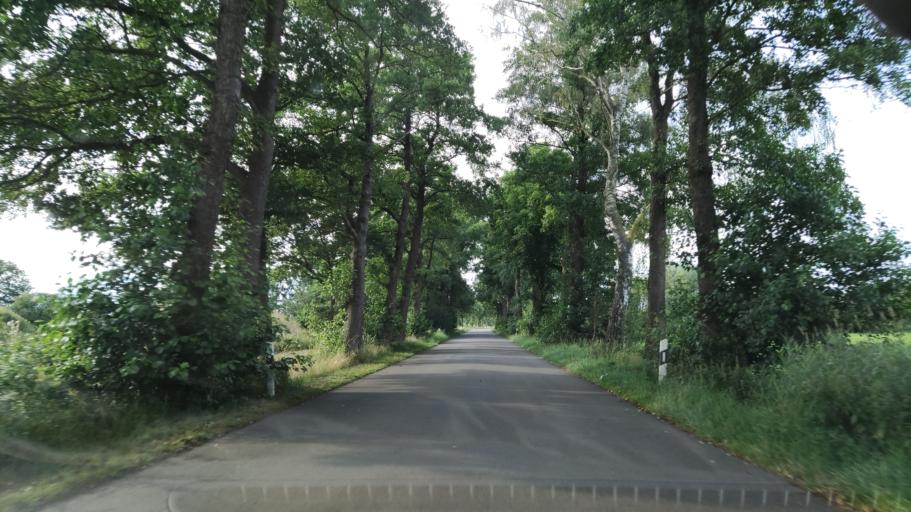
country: DE
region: Lower Saxony
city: Dannenberg
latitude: 53.0790
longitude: 11.1060
